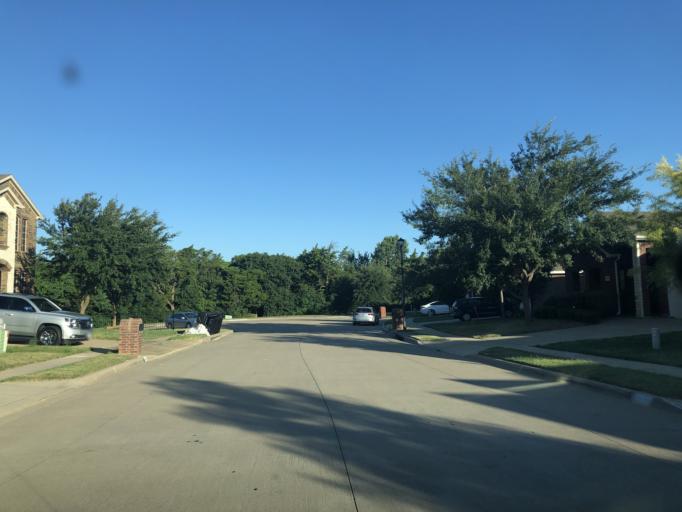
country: US
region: Texas
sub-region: Dallas County
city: Duncanville
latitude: 32.6500
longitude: -96.9499
